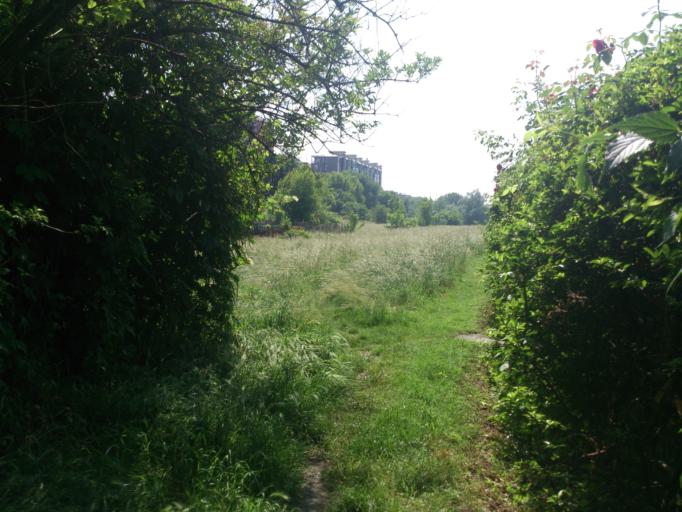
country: IT
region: Lombardy
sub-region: Citta metropolitana di Milano
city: Civesio
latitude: 45.4050
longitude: 9.2643
